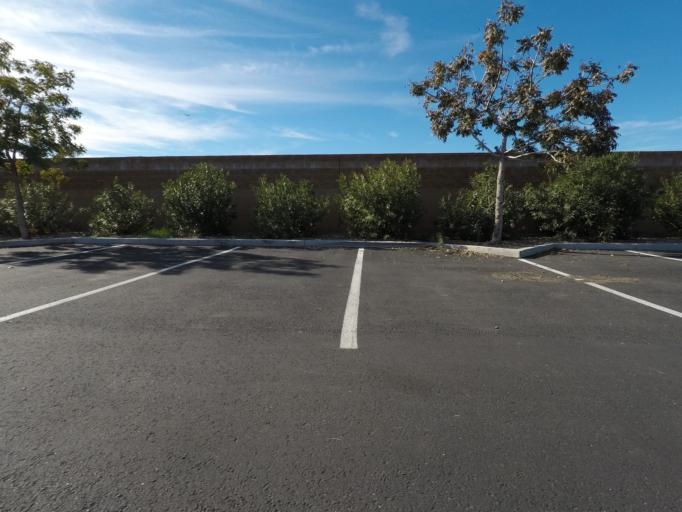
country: US
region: Arizona
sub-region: Maricopa County
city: Tempe
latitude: 33.4340
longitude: -111.8785
